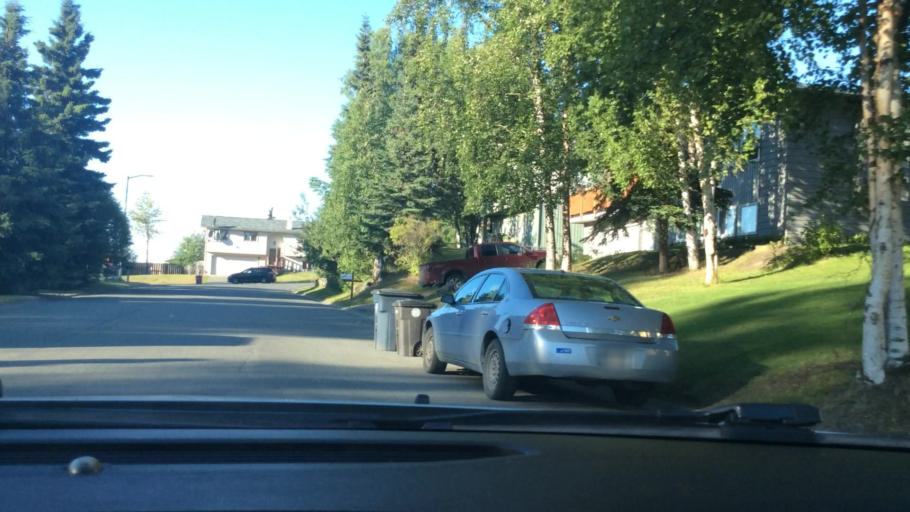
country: US
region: Alaska
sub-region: Anchorage Municipality
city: Anchorage
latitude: 61.2160
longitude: -149.7688
